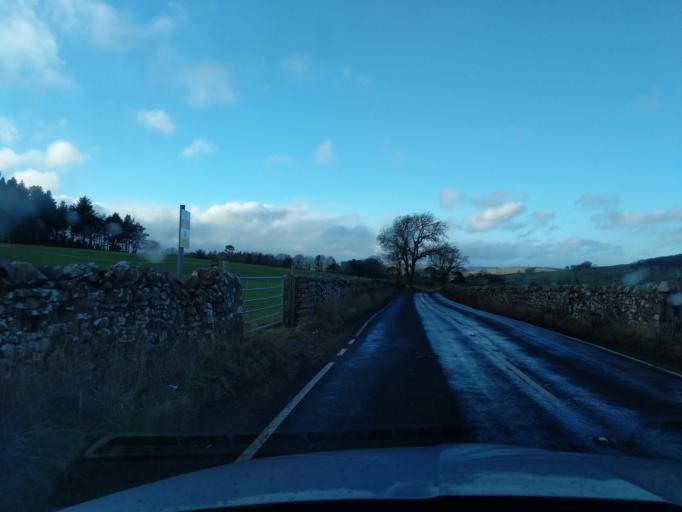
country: GB
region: England
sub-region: North Yorkshire
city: Leyburn
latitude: 54.3520
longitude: -1.8105
